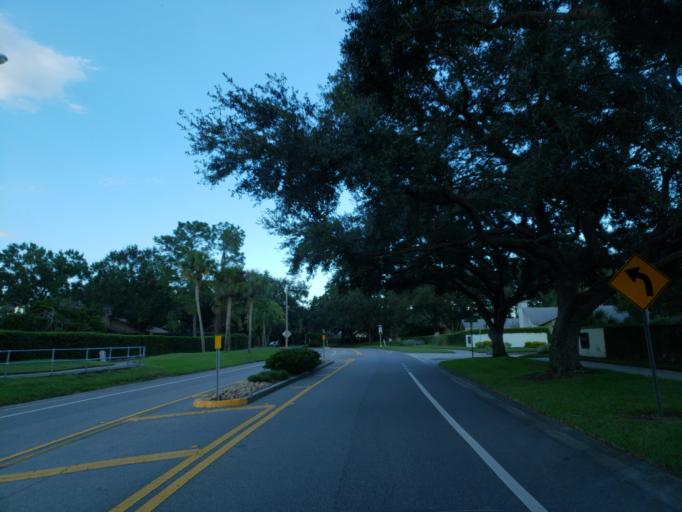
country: US
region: Florida
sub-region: Hillsborough County
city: Carrollwood Village
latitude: 28.0741
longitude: -82.5208
